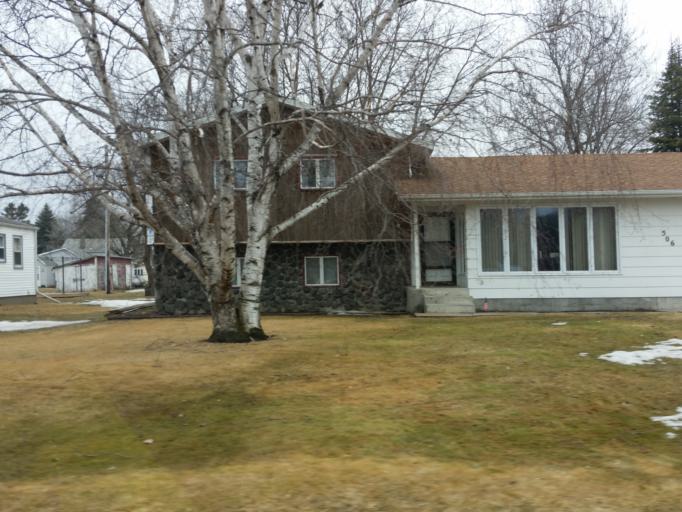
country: US
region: North Dakota
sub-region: Walsh County
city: Grafton
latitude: 48.5668
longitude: -97.1750
